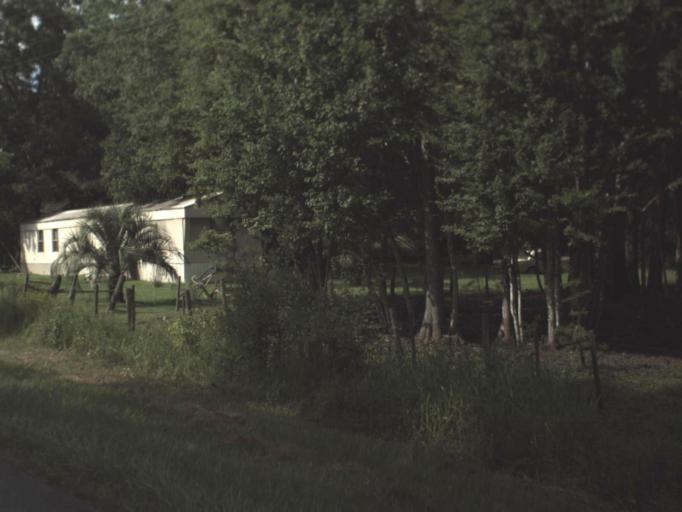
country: US
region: Florida
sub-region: Taylor County
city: Perry
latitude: 30.3491
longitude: -83.6501
